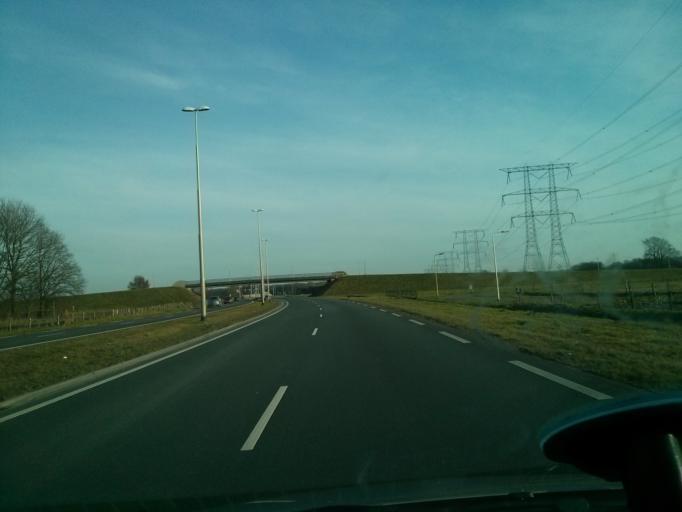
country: NL
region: North Brabant
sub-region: Gemeente Loon op Zand
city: Loon op Zand
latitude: 51.5957
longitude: 5.0995
